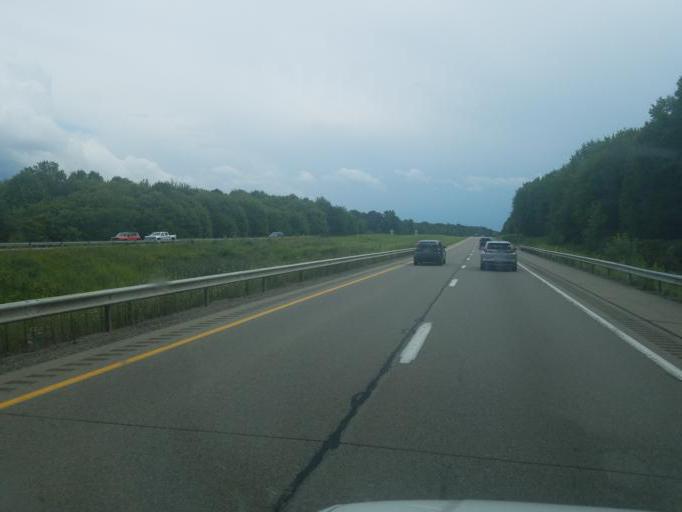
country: US
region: Pennsylvania
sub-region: Crawford County
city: Cochranton
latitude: 41.5036
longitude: -80.1700
